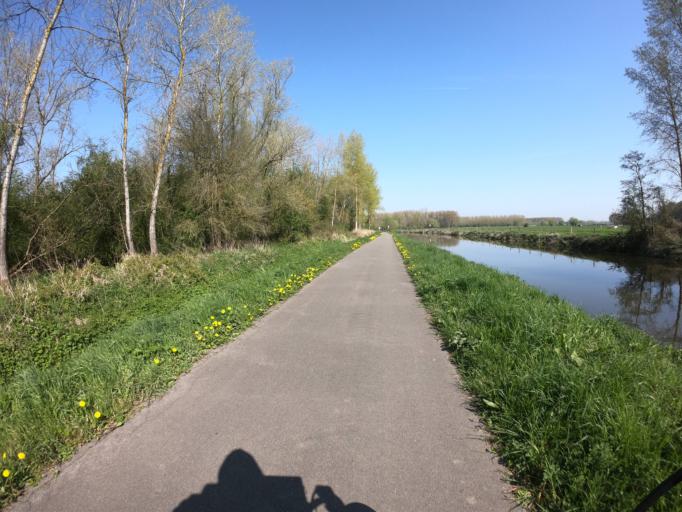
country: BE
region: Flanders
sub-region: Provincie Oost-Vlaanderen
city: Geraardsbergen
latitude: 50.7459
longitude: 3.8562
